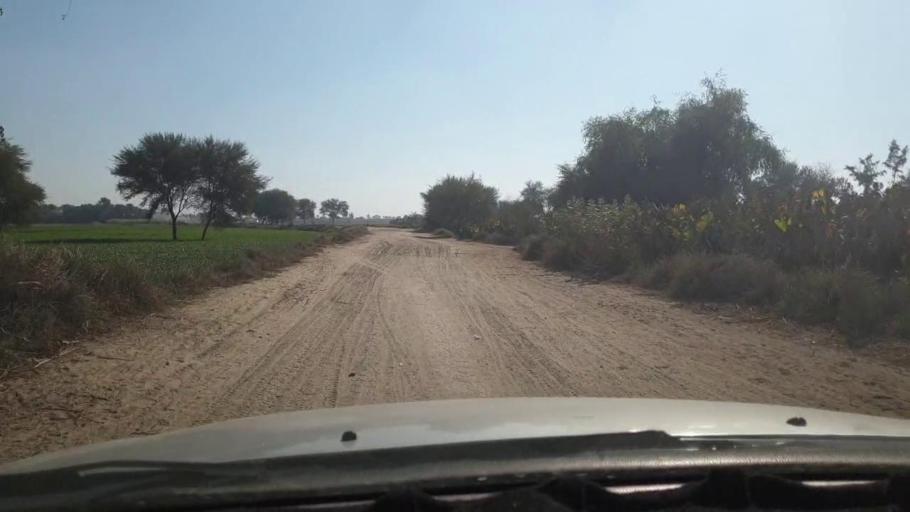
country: PK
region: Sindh
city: Ghotki
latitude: 28.0214
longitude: 69.2224
